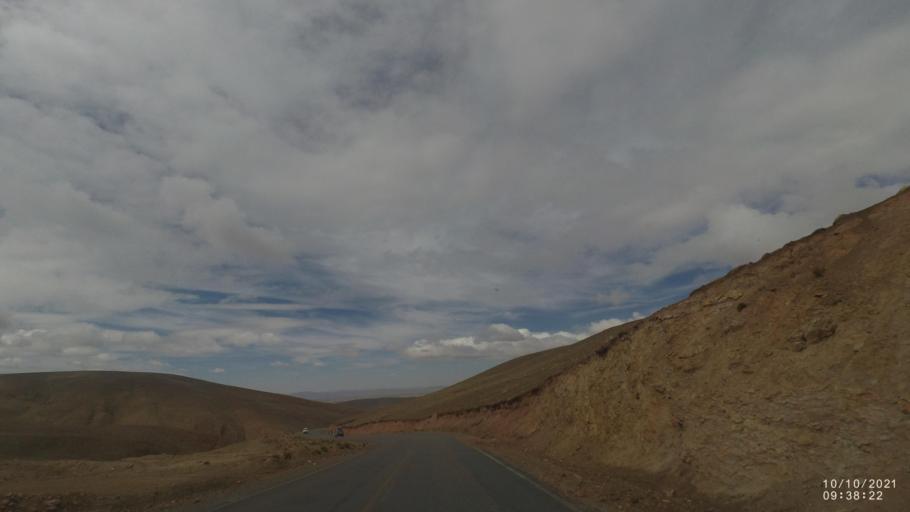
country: BO
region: La Paz
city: Quime
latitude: -17.1322
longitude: -67.3393
